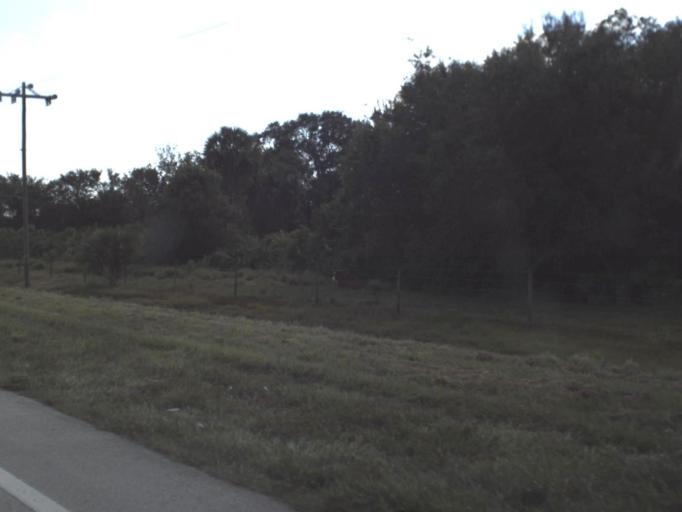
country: US
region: Florida
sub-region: Okeechobee County
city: Okeechobee
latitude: 27.3160
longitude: -80.9106
